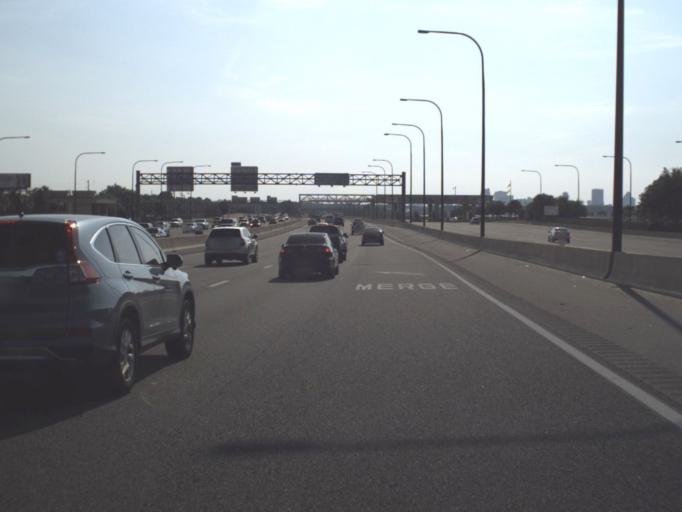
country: US
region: Florida
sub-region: Orange County
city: Azalea Park
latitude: 28.5399
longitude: -81.3214
